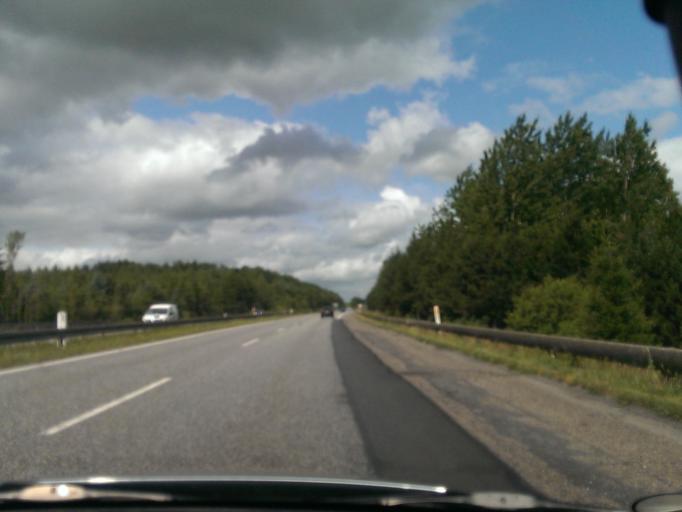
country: DK
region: North Denmark
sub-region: Mariagerfjord Kommune
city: Hobro
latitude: 56.5813
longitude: 9.7979
